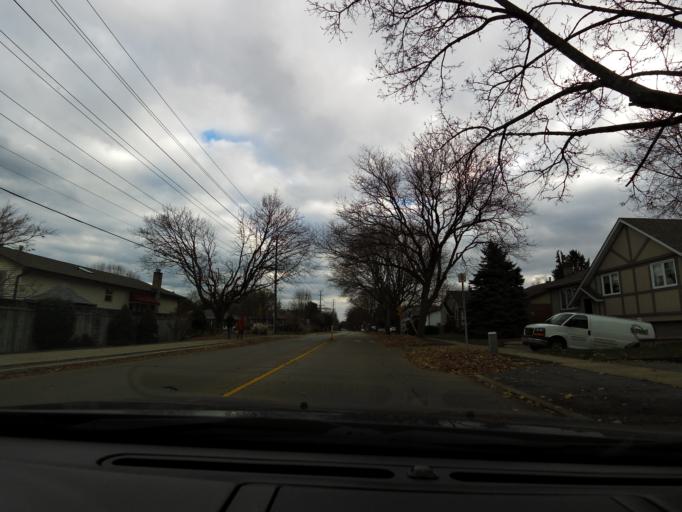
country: CA
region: Ontario
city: Burlington
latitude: 43.3190
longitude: -79.8204
